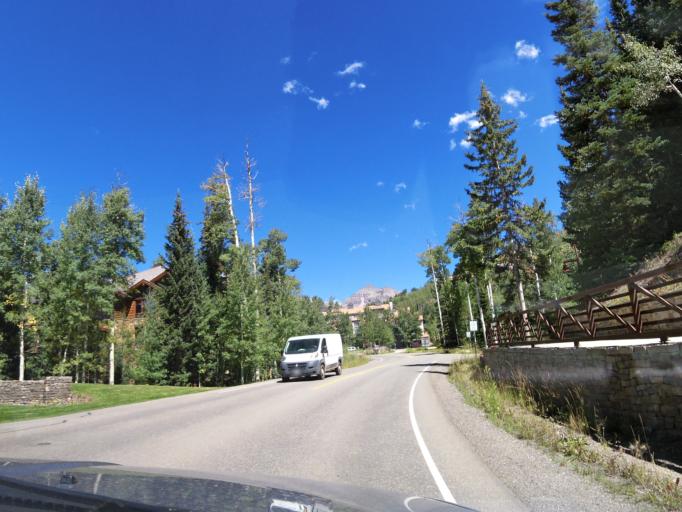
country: US
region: Colorado
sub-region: San Miguel County
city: Mountain Village
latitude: 37.9343
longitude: -107.8488
